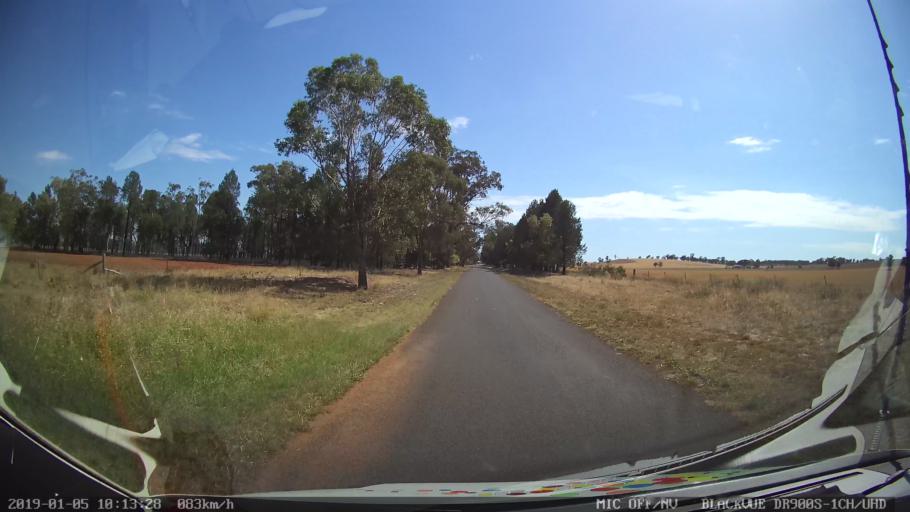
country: AU
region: New South Wales
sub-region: Gilgandra
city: Gilgandra
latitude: -31.6022
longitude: 148.9252
